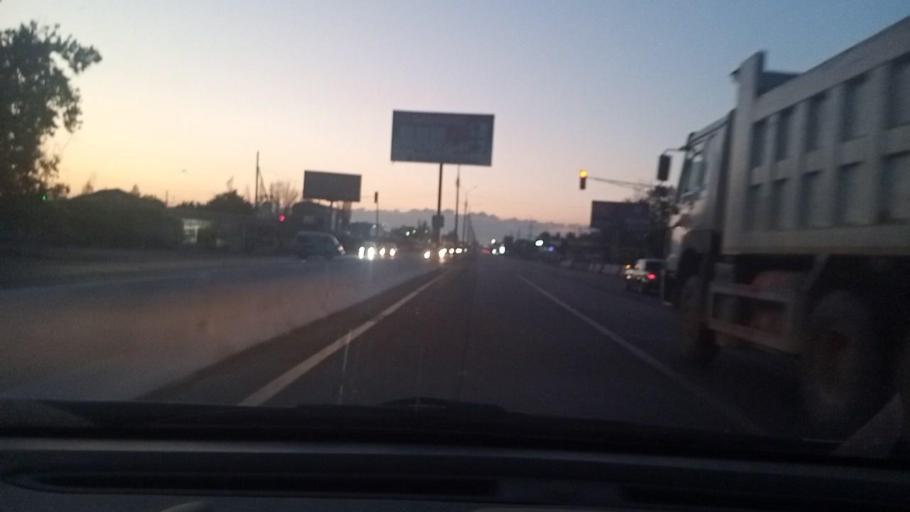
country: UZ
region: Toshkent Shahri
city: Tashkent
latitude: 41.2438
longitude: 69.2238
